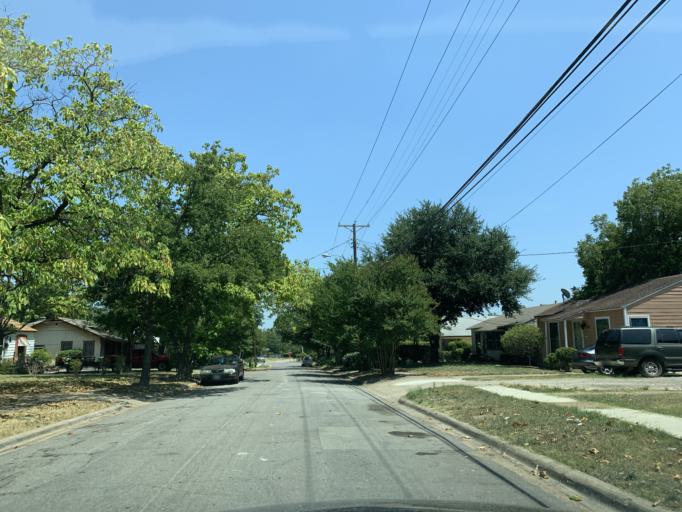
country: US
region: Texas
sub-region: Dallas County
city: Dallas
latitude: 32.6927
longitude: -96.8010
